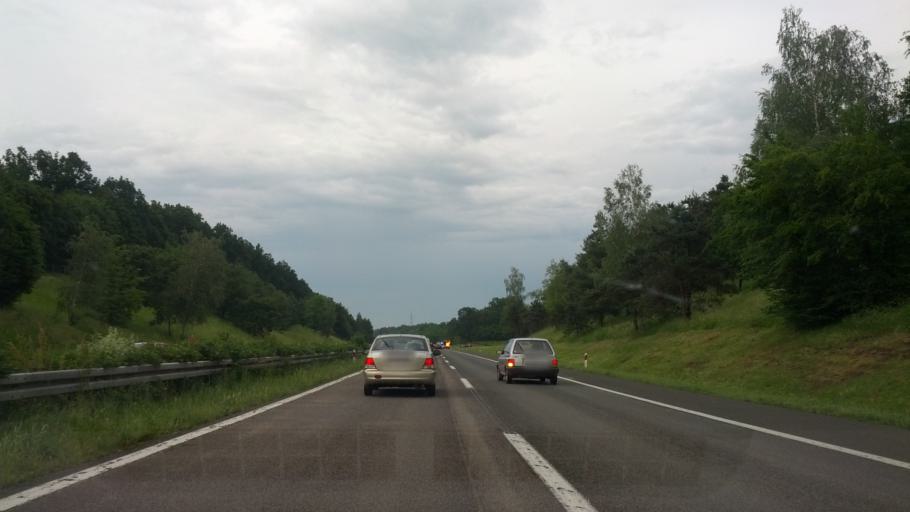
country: HR
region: Grad Zagreb
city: Horvati
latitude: 45.6840
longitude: 15.7940
